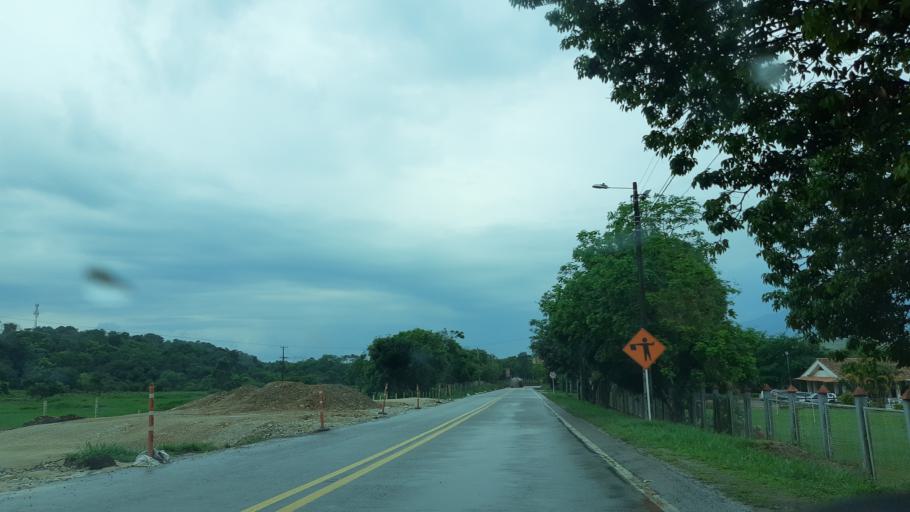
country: CO
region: Casanare
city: Monterrey
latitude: 4.8867
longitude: -72.8962
